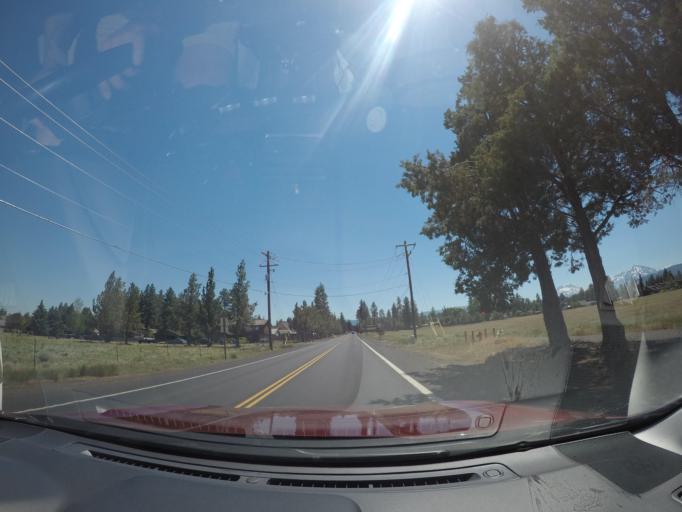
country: US
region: Oregon
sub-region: Deschutes County
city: Sisters
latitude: 44.2954
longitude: -121.5437
